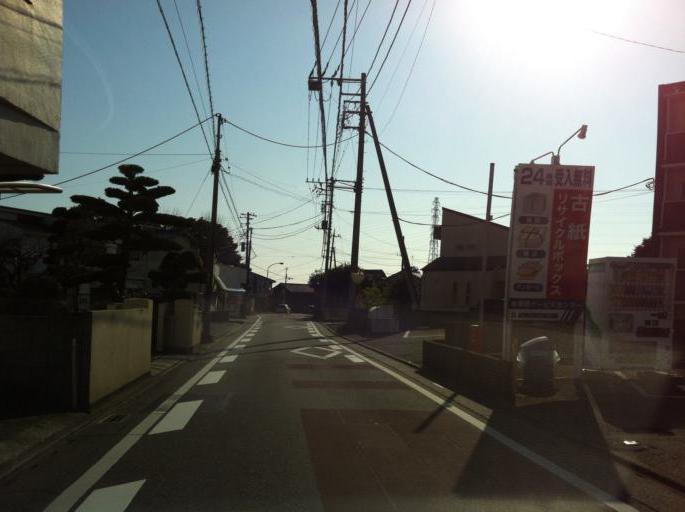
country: JP
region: Shizuoka
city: Mishima
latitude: 35.1294
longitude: 138.8865
